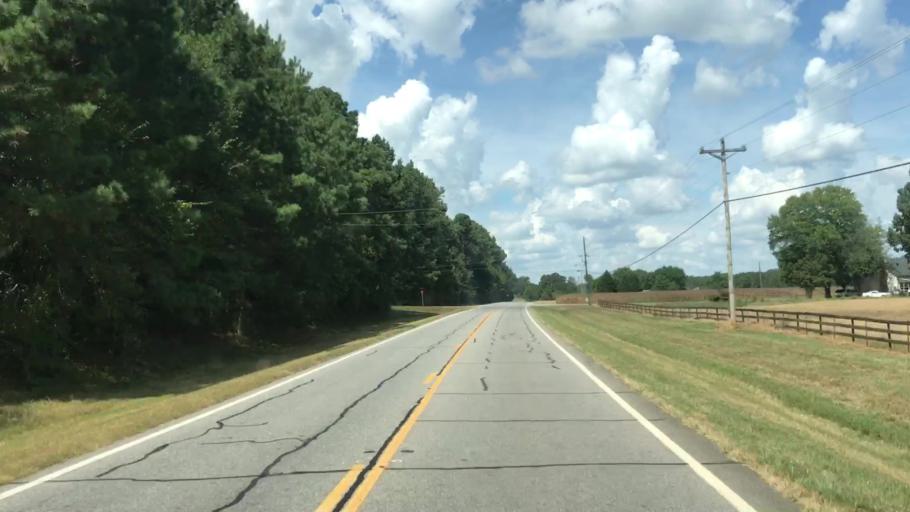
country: US
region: Georgia
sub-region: Oconee County
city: Watkinsville
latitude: 33.8126
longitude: -83.3580
